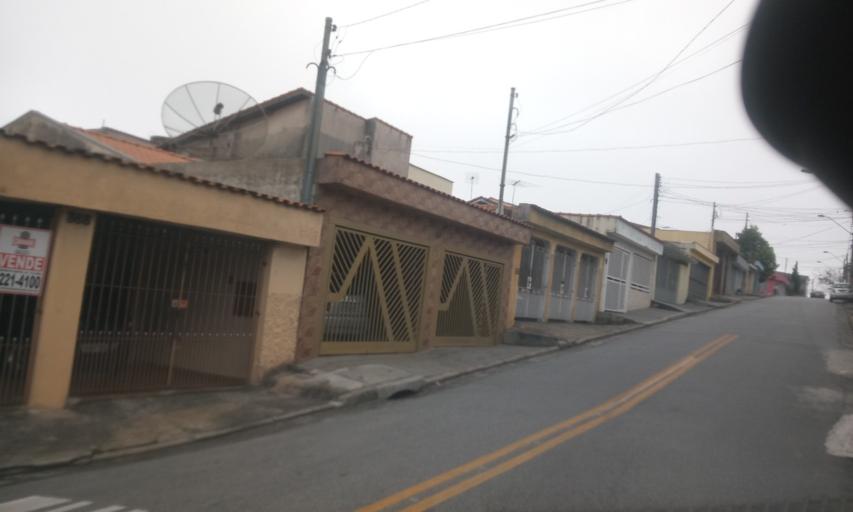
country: BR
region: Sao Paulo
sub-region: Sao Caetano Do Sul
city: Sao Caetano do Sul
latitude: -23.6412
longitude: -46.5693
